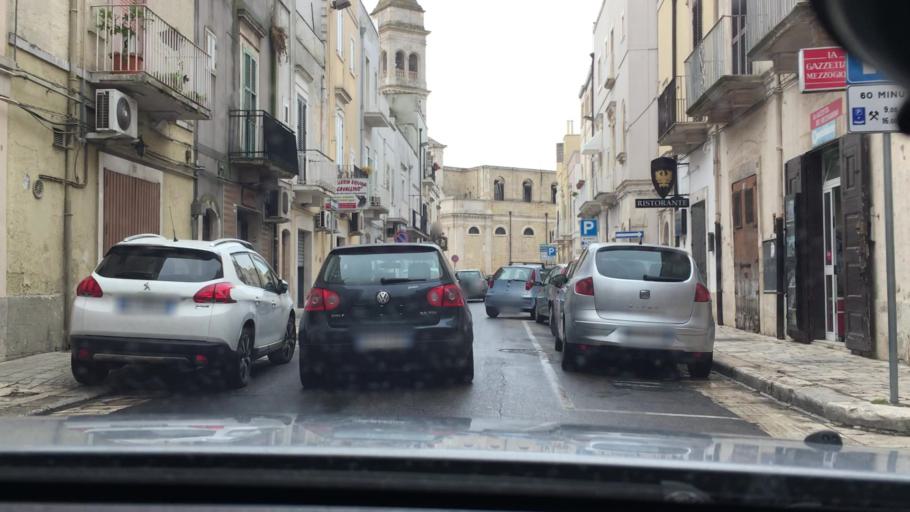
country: IT
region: Apulia
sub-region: Provincia di Bari
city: Gioia del Colle
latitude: 40.8016
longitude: 16.9225
